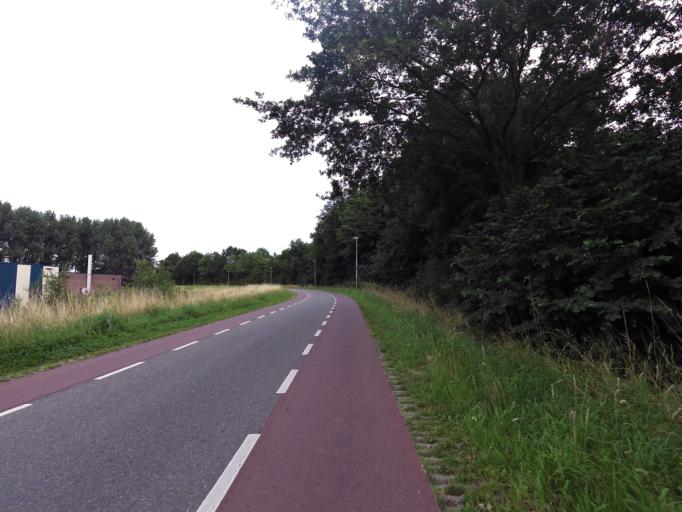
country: NL
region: Gelderland
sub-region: Gemeente Doesburg
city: Doesburg
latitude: 52.0002
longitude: 6.1425
